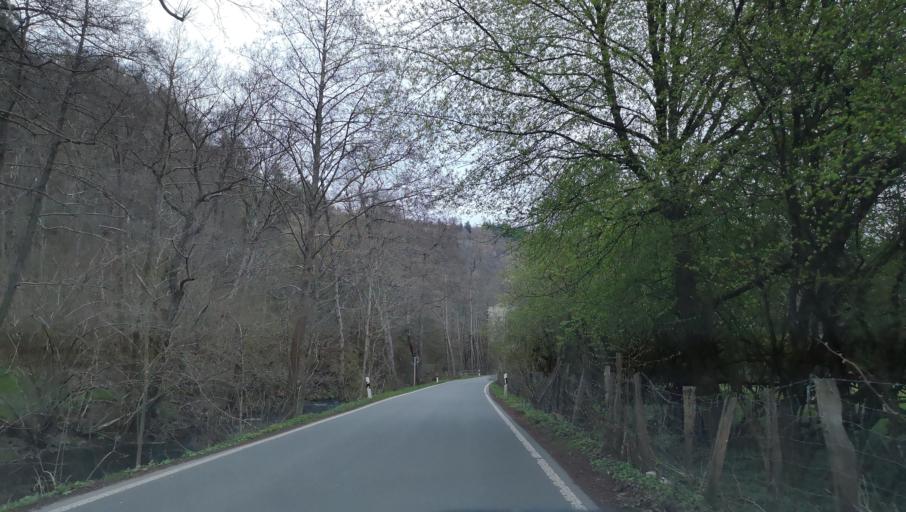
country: DE
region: North Rhine-Westphalia
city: Ennepetal
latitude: 51.2919
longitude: 7.3815
